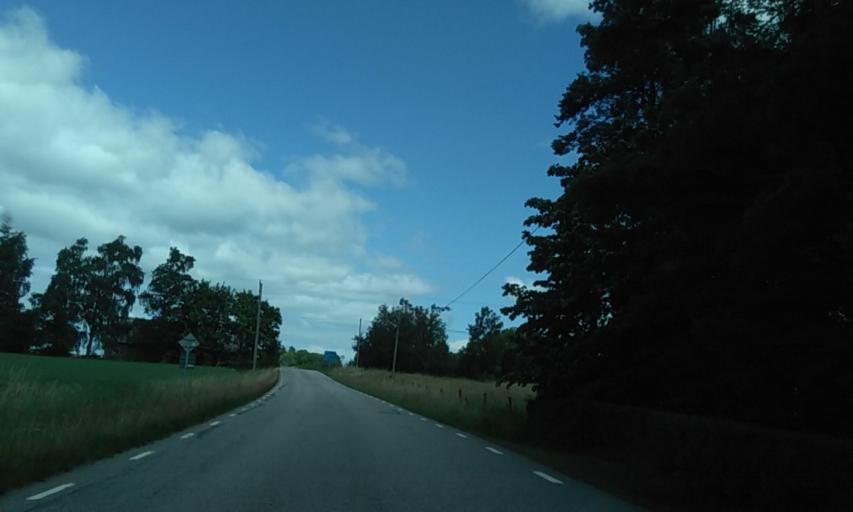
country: SE
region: Vaestra Goetaland
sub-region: Grastorps Kommun
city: Graestorp
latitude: 58.3738
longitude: 12.6917
